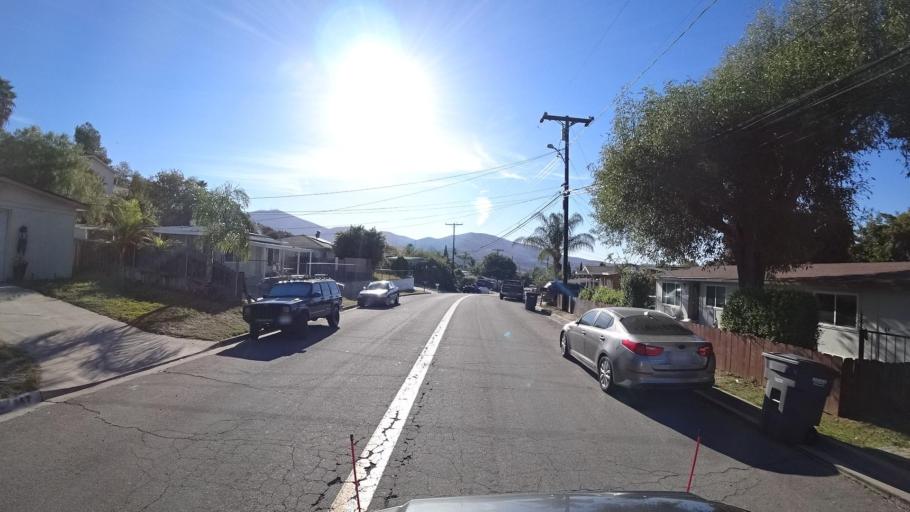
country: US
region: California
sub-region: San Diego County
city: La Presa
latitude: 32.7119
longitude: -116.9896
